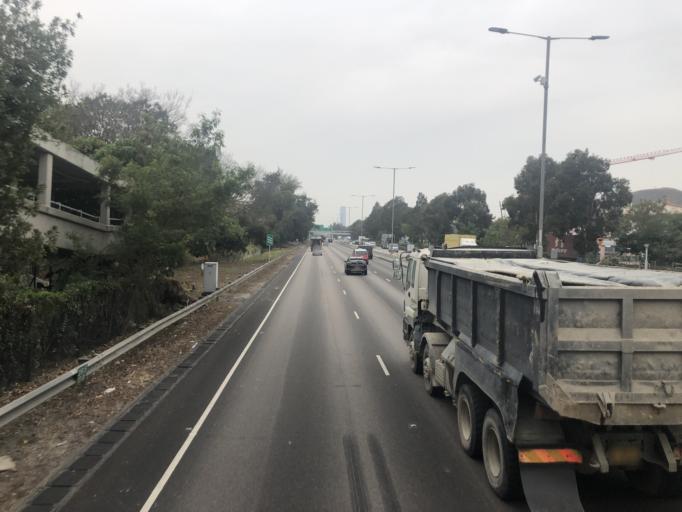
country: CN
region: Guangdong
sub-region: Shenzhen
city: Shenzhen
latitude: 22.5035
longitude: 114.0995
